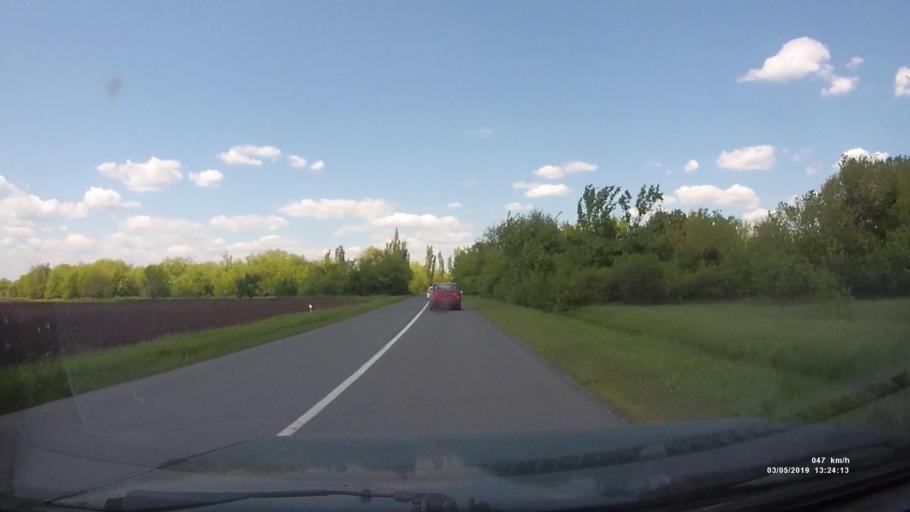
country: RU
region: Rostov
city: Semikarakorsk
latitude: 47.5630
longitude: 40.7951
